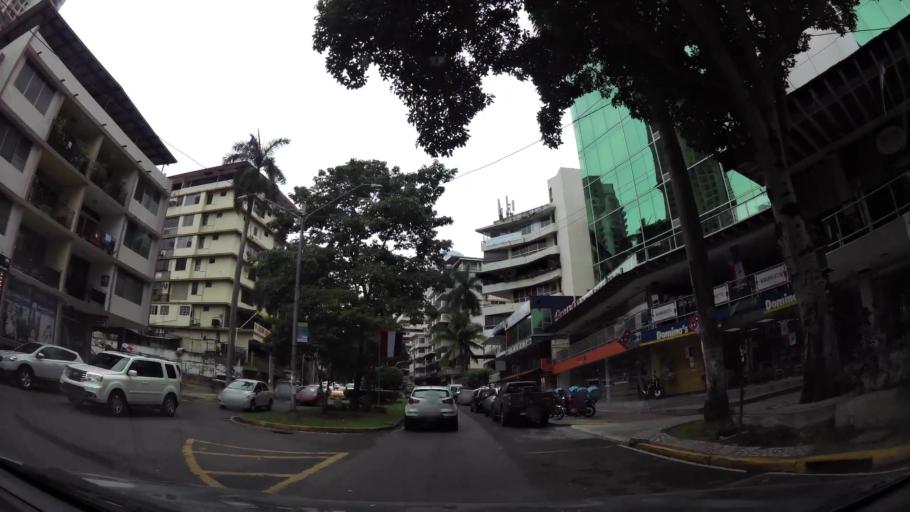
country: PA
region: Panama
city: Panama
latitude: 8.9891
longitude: -79.5273
